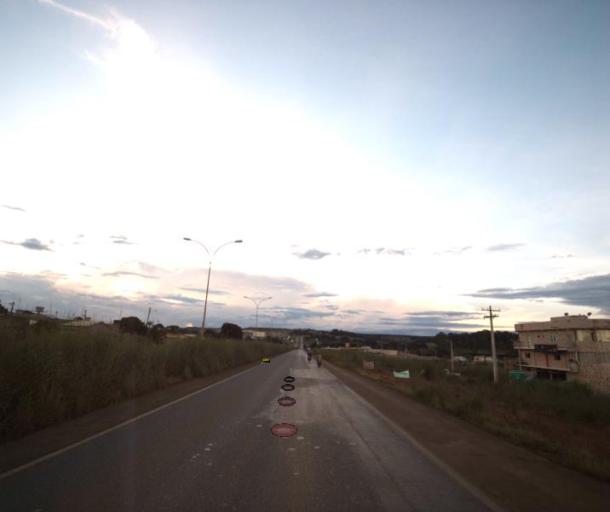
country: BR
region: Goias
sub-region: Anapolis
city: Anapolis
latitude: -16.2764
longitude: -48.9665
